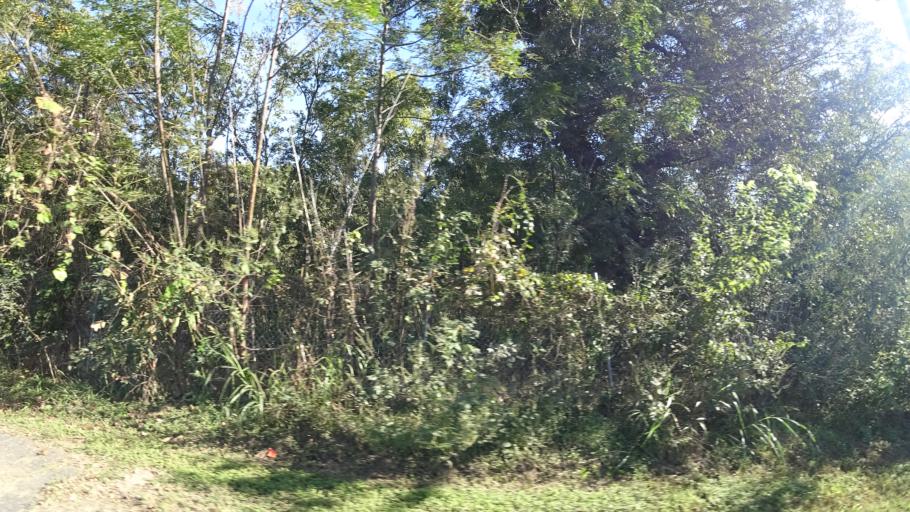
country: US
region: Texas
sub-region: Travis County
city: Hornsby Bend
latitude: 30.2643
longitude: -97.6587
